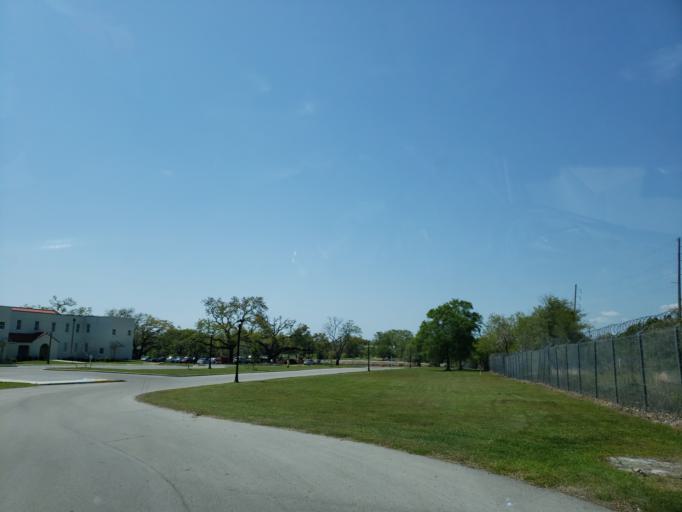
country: US
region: Mississippi
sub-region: Harrison County
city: Gulfport
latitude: 30.3796
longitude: -89.0531
